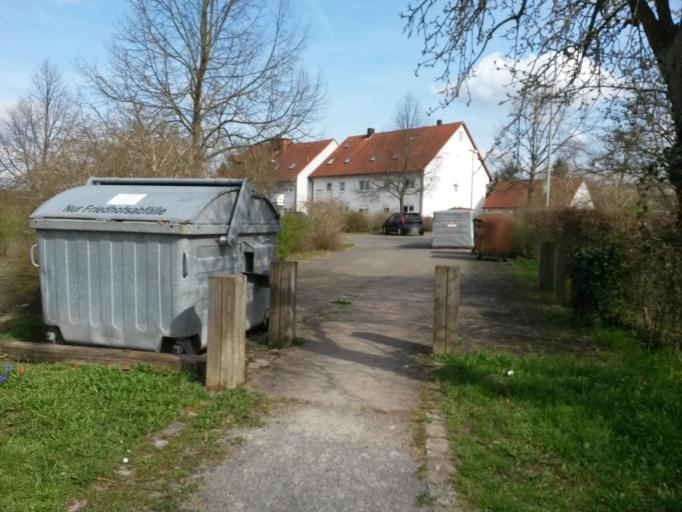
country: DE
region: Bavaria
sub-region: Regierungsbezirk Unterfranken
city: Gerolzhofen
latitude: 49.9029
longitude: 10.3520
